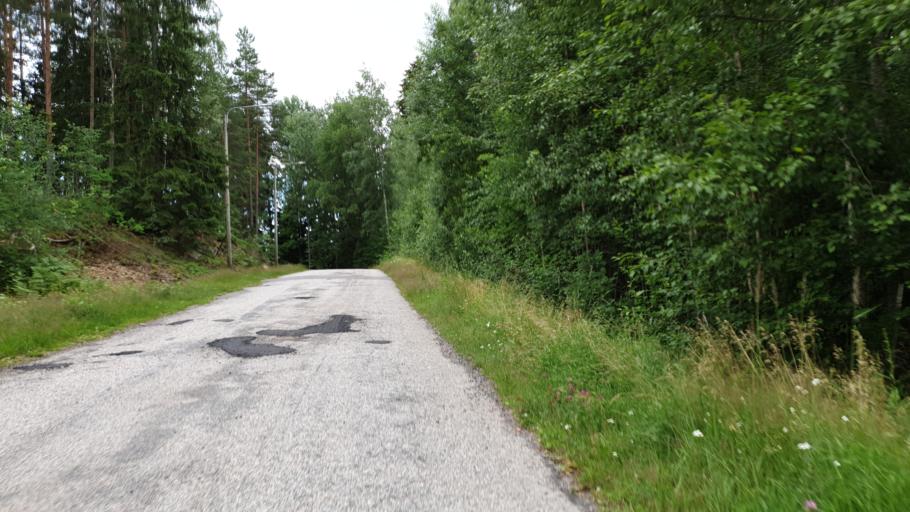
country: FI
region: Uusimaa
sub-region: Helsinki
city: Teekkarikylae
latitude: 60.2808
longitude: 24.9015
